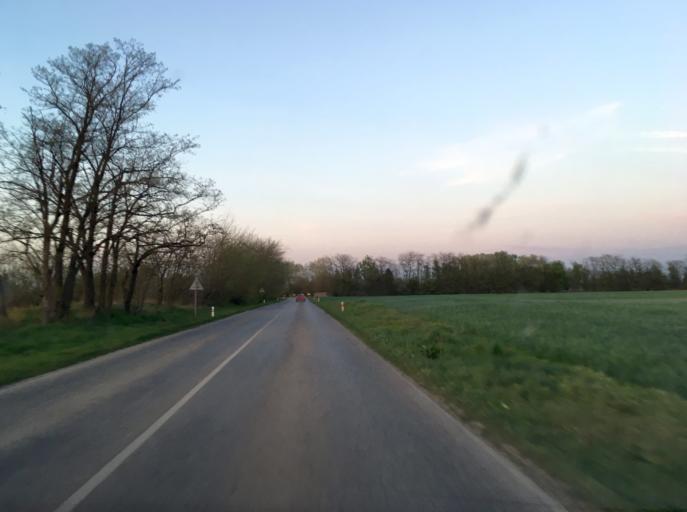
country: SK
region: Nitriansky
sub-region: Okres Nove Zamky
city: Nove Zamky
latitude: 47.9565
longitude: 18.1433
